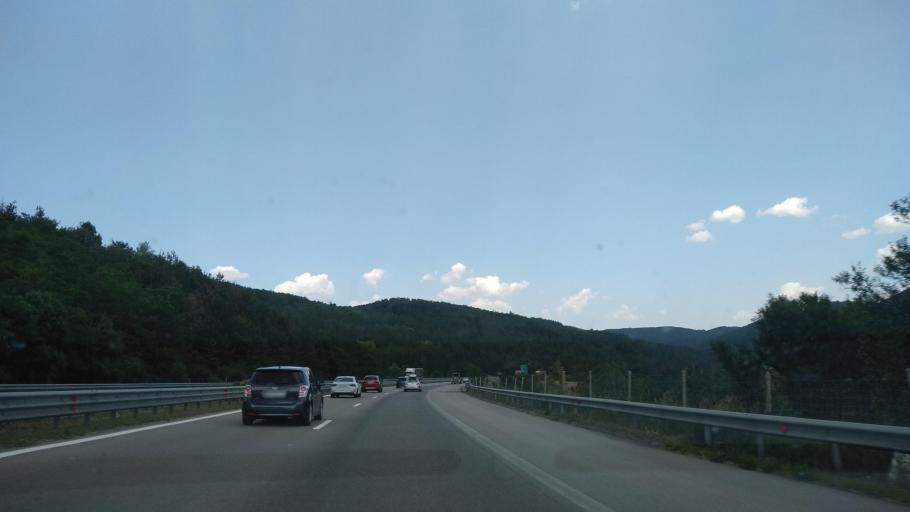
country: BG
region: Sofia-Capital
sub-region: Stolichna Obshtina
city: Bukhovo
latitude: 42.7284
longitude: 23.5471
